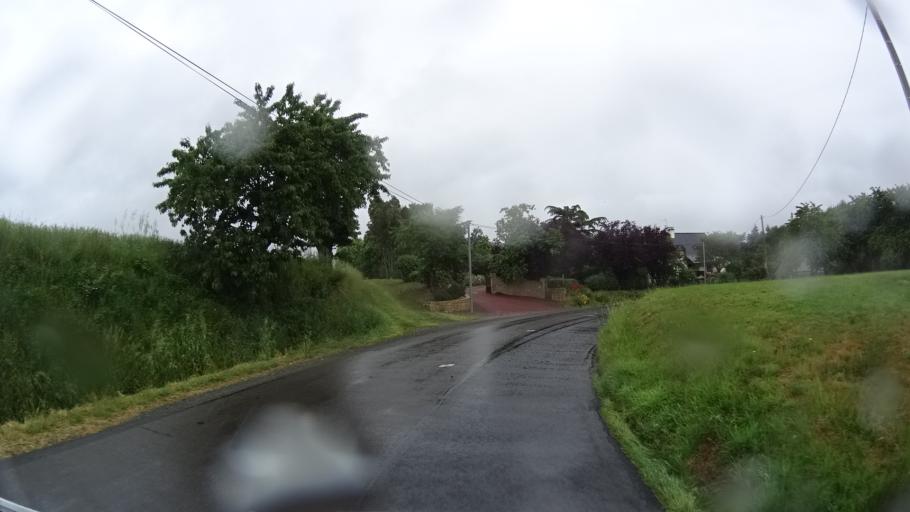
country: FR
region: Brittany
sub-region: Departement d'Ille-et-Vilaine
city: Saint-Erblon
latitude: 48.0353
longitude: -1.6293
